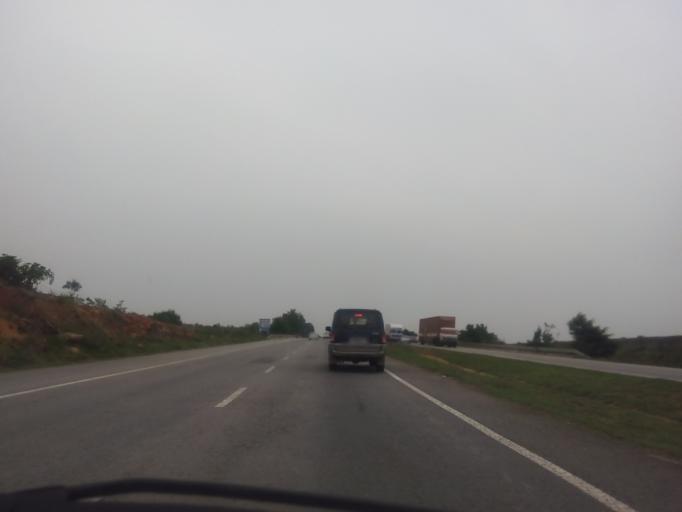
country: IN
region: Karnataka
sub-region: Bangalore Urban
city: Bangalore
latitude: 12.9266
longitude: 77.4695
